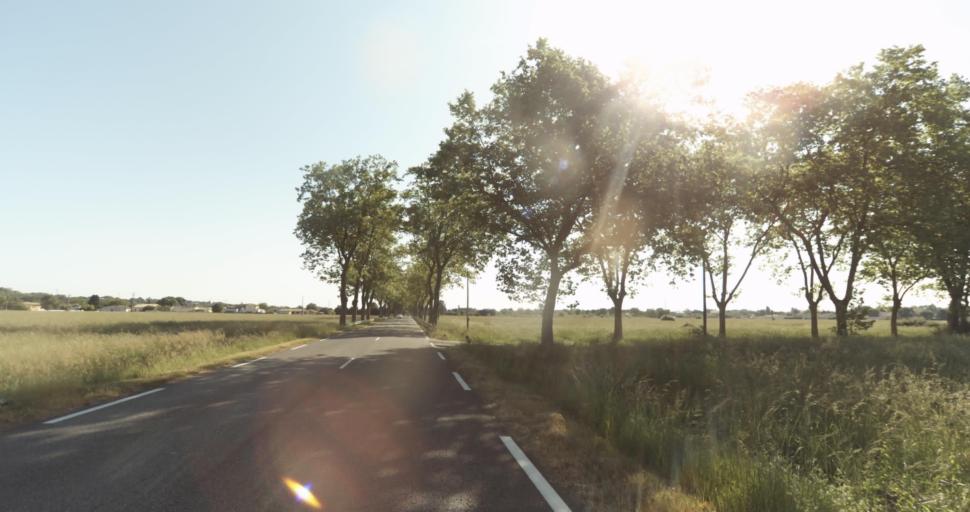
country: FR
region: Midi-Pyrenees
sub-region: Departement de la Haute-Garonne
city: La Salvetat-Saint-Gilles
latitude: 43.5549
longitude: 1.2708
